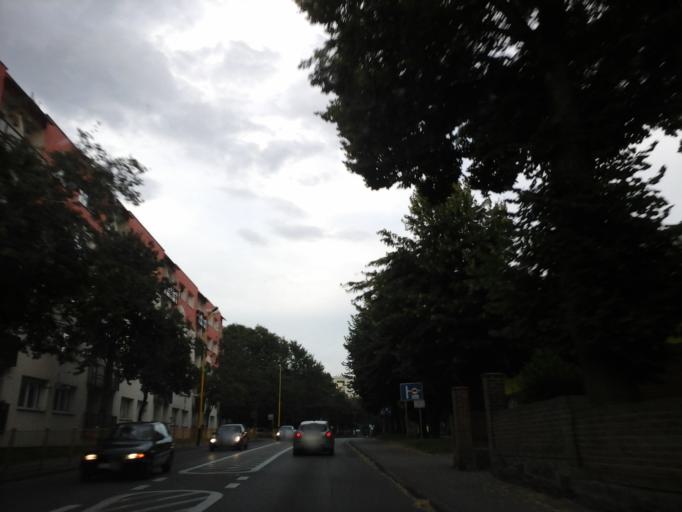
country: PL
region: West Pomeranian Voivodeship
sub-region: Powiat goleniowski
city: Nowogard
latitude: 53.6724
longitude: 15.1180
